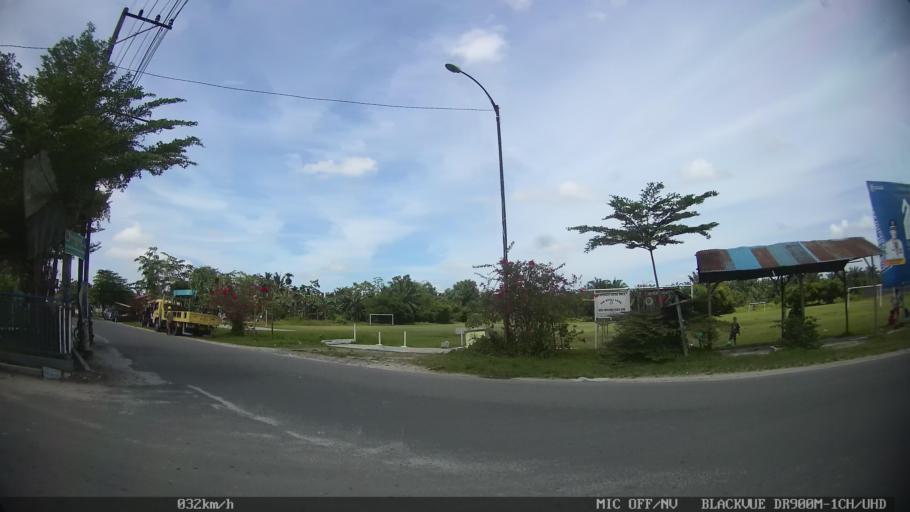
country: ID
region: North Sumatra
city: Percut
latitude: 3.5889
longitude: 98.8833
